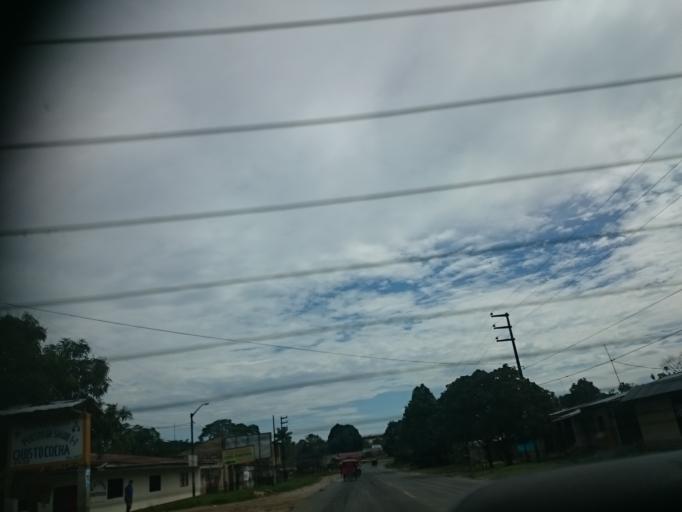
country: PE
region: Loreto
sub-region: Provincia de Maynas
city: Iquitos
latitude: -3.8227
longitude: -73.3256
